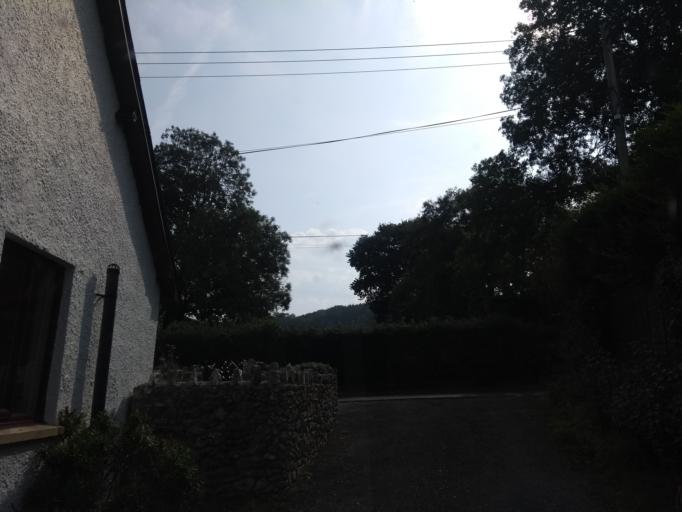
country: GB
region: England
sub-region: Somerset
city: Chard
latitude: 50.8821
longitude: -3.0430
